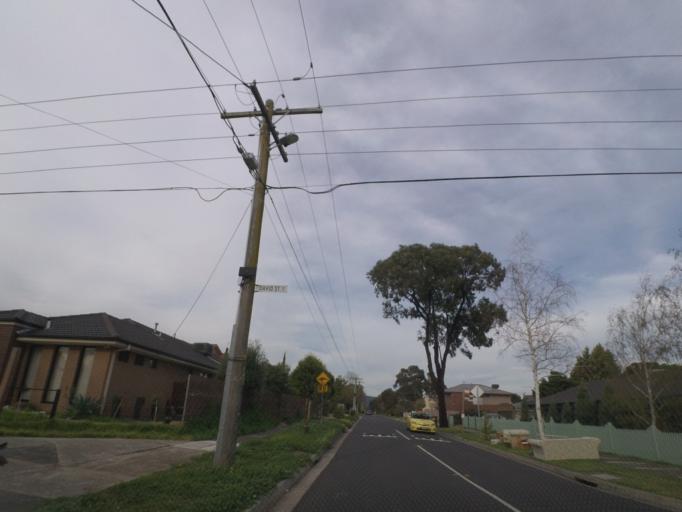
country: AU
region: Victoria
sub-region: Knox
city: Knoxfield
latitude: -37.8887
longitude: 145.2513
